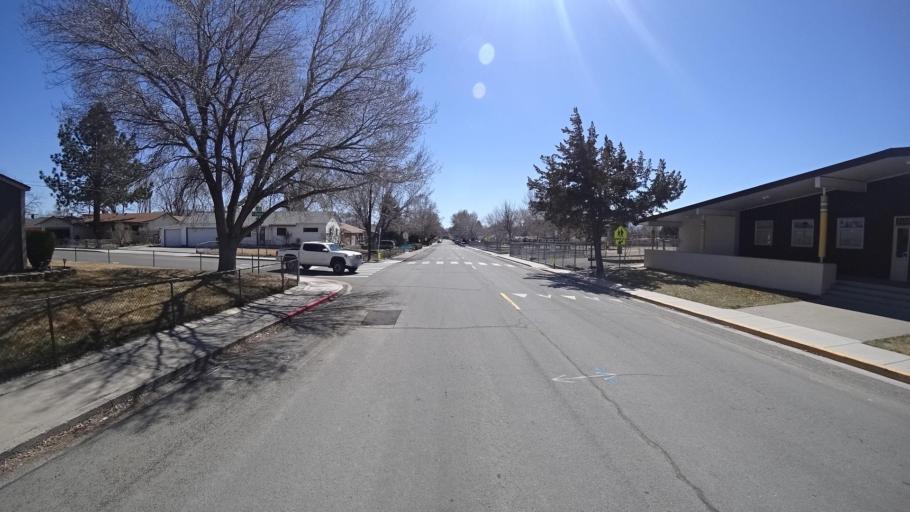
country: US
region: Nevada
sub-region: Washoe County
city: Sparks
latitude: 39.5555
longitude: -119.7484
